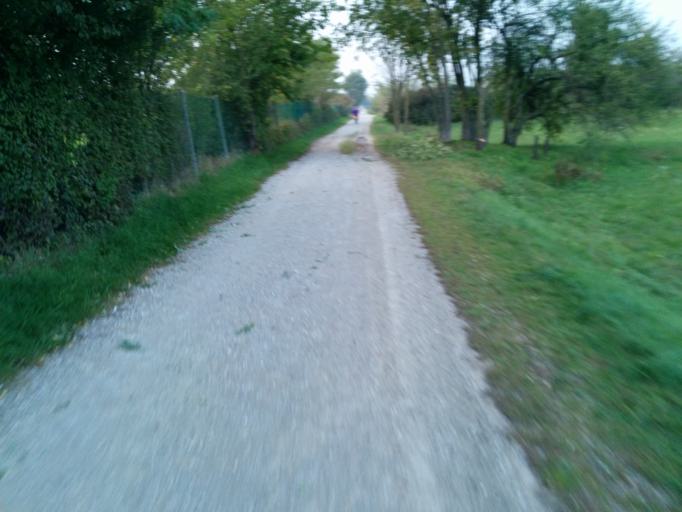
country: IT
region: Friuli Venezia Giulia
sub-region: Provincia di Udine
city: Povoletto
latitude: 46.0963
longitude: 13.2761
